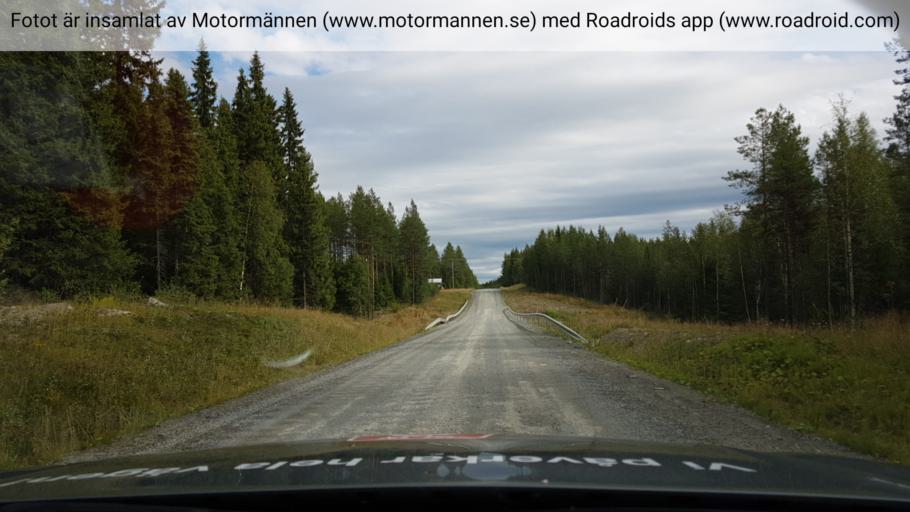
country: SE
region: Jaemtland
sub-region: Krokoms Kommun
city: Valla
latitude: 63.6476
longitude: 13.8168
